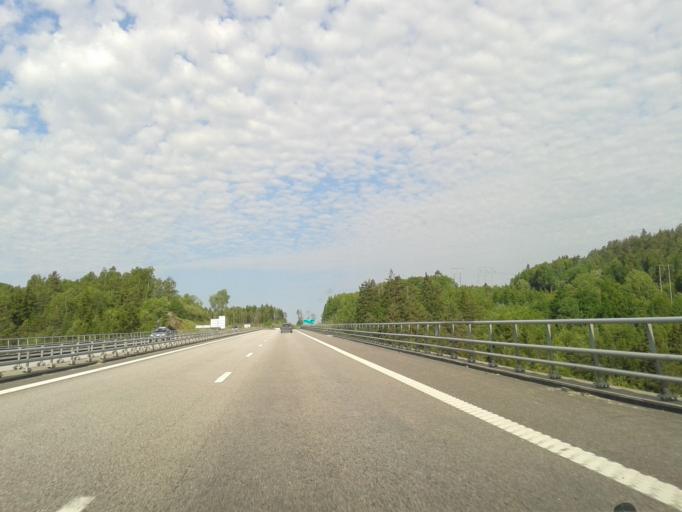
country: SE
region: Vaestra Goetaland
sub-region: Munkedals Kommun
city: Munkedal
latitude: 58.4458
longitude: 11.6857
